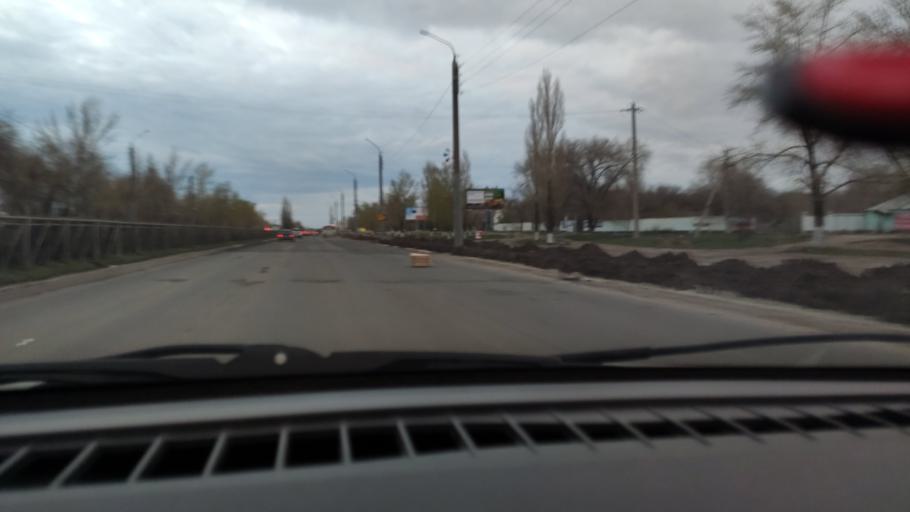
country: RU
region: Orenburg
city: Orenburg
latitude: 51.8195
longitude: 55.1077
